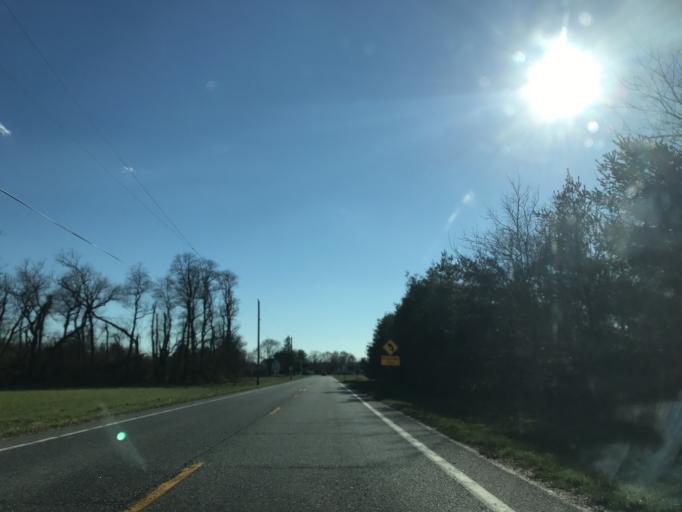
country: US
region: Maryland
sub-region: Caroline County
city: Ridgely
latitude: 39.0372
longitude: -75.8724
